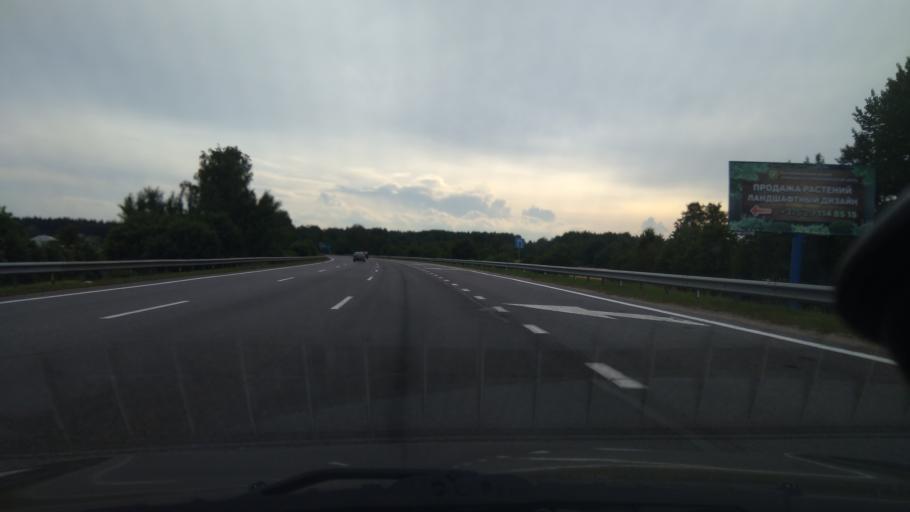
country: BY
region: Minsk
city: Azyartso
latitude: 53.8035
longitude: 27.3802
